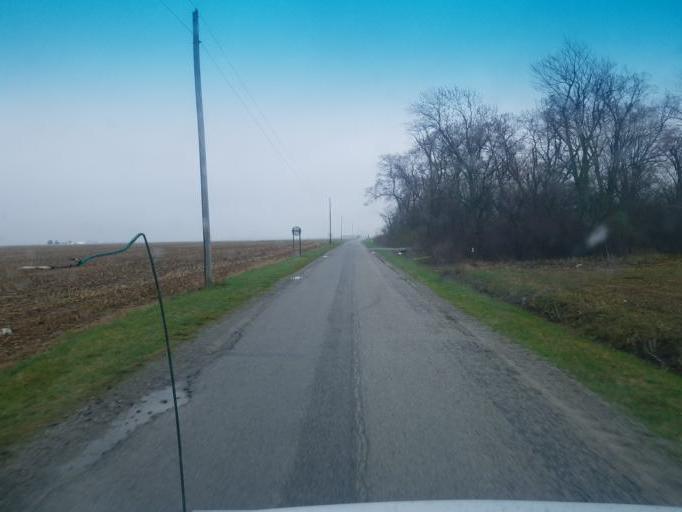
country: US
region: Ohio
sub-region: Wood County
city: North Baltimore
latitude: 41.2685
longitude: -83.6431
